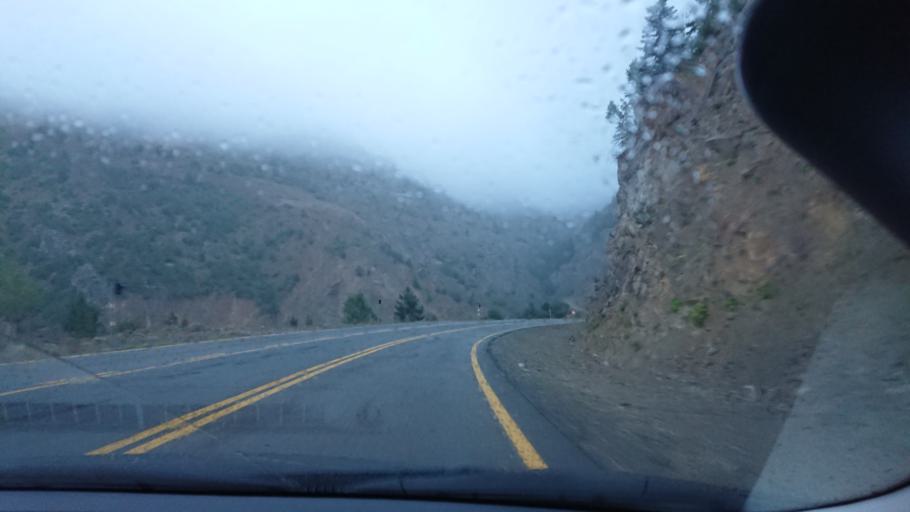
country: TR
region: Gumushane
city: Torul
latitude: 40.6526
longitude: 39.3618
